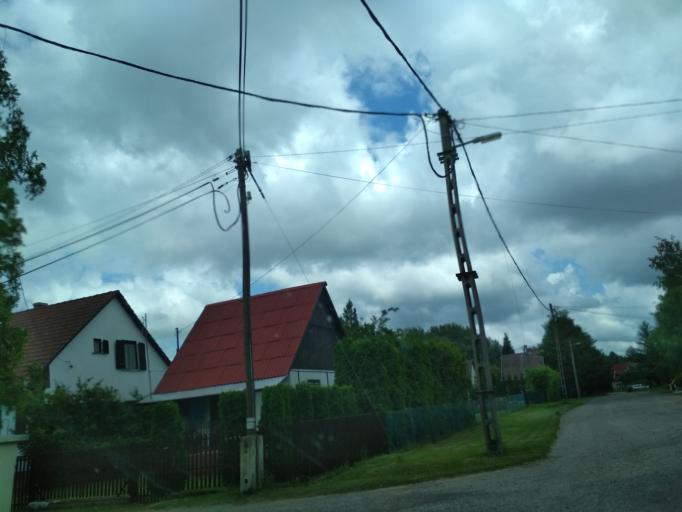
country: HU
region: Jasz-Nagykun-Szolnok
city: Tiszafured
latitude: 47.6178
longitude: 20.7368
